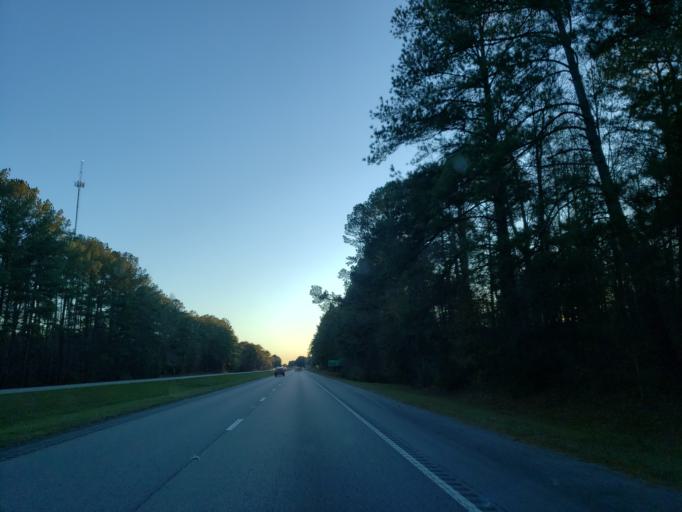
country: US
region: Mississippi
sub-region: Clarke County
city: Stonewall
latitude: 32.2107
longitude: -88.8398
